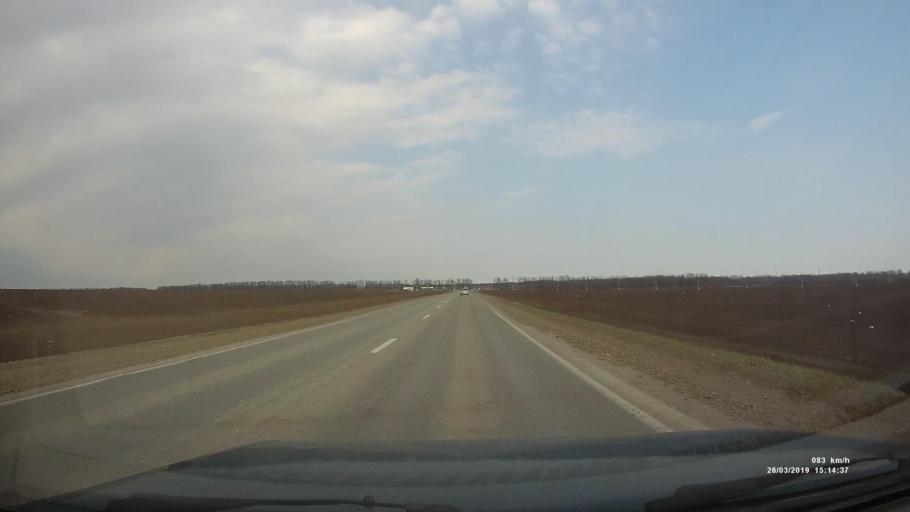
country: RU
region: Rostov
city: Taganrog
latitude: 47.2825
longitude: 38.8708
